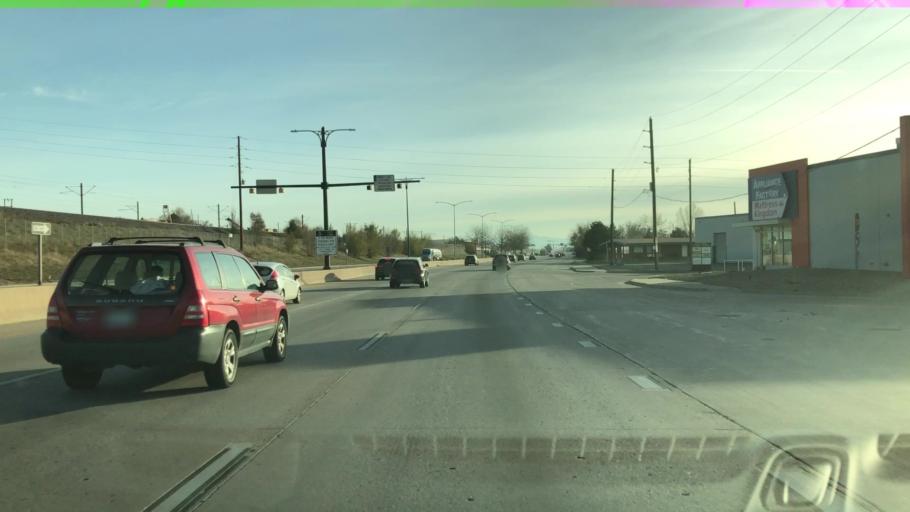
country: US
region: Colorado
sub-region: Arapahoe County
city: Englewood
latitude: 39.6651
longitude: -104.9969
